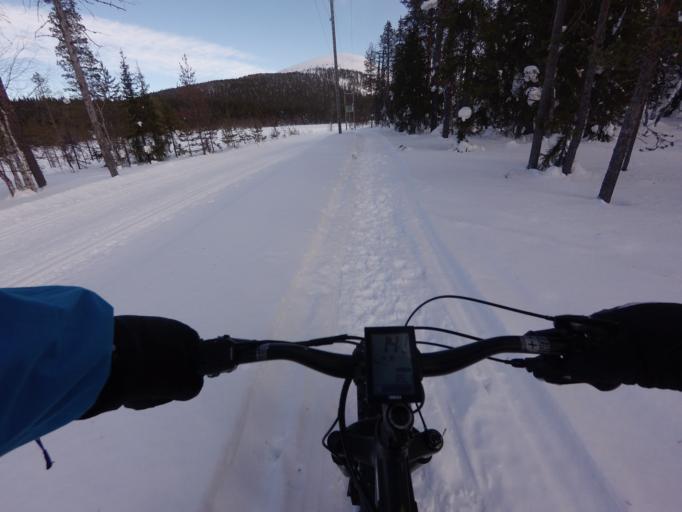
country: FI
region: Lapland
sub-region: Tunturi-Lappi
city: Kolari
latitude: 67.6017
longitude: 24.2191
